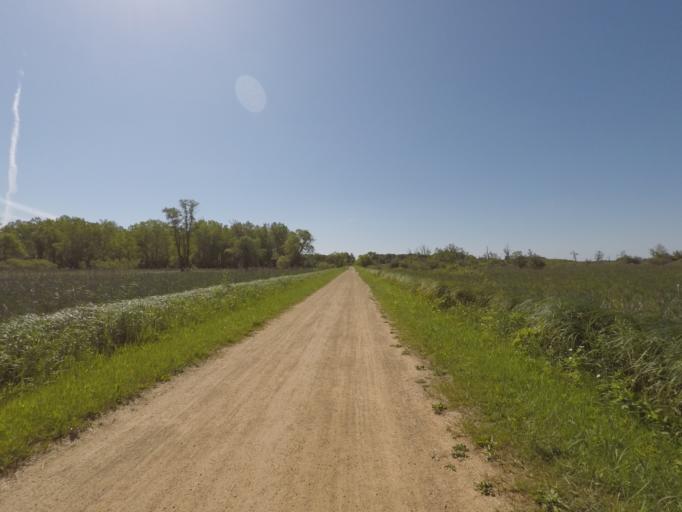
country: US
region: Wisconsin
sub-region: Dane County
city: Verona
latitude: 42.9830
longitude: -89.5627
